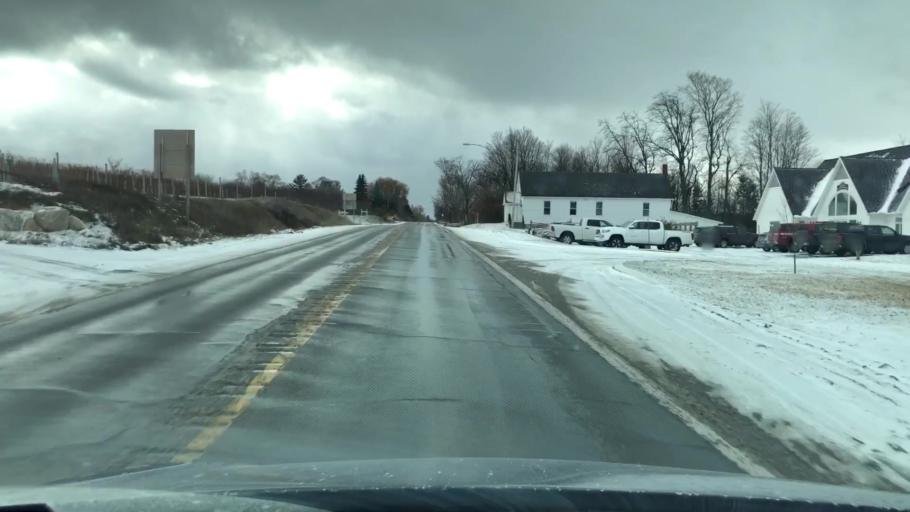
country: US
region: Michigan
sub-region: Antrim County
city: Elk Rapids
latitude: 44.8812
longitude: -85.5154
